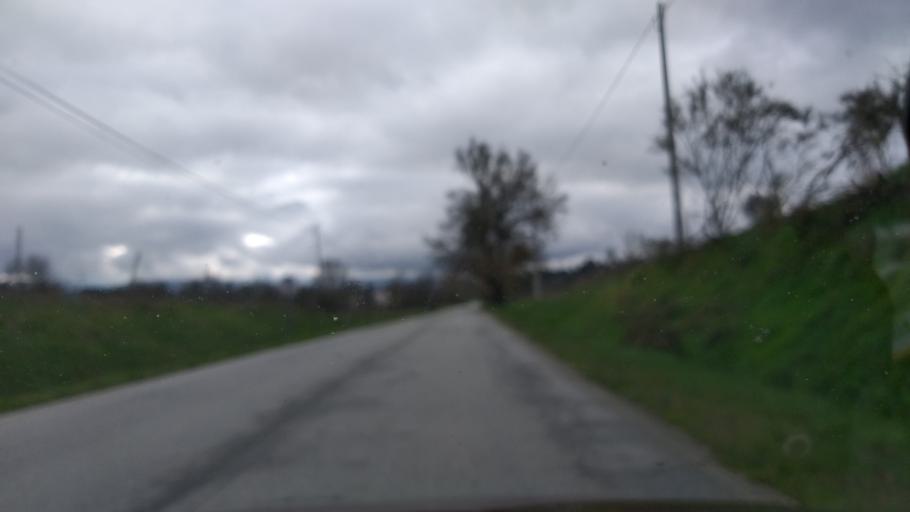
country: PT
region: Guarda
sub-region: Celorico da Beira
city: Celorico da Beira
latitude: 40.6884
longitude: -7.3731
